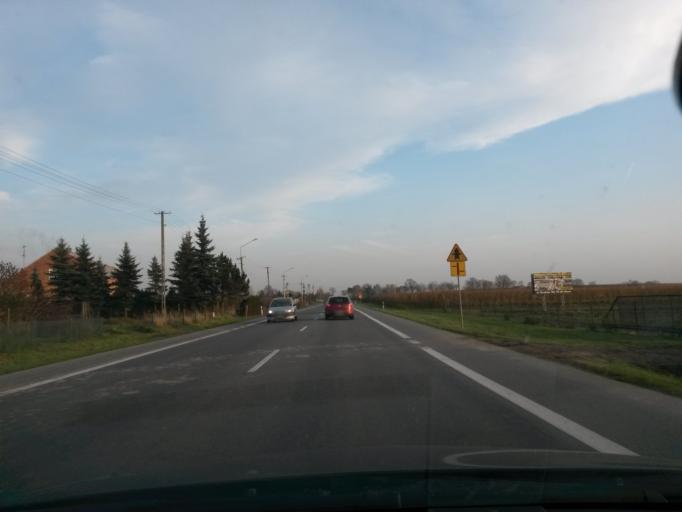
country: PL
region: Lodz Voivodeship
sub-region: Powiat wielunski
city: Czarnozyly
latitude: 51.2566
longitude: 18.4935
